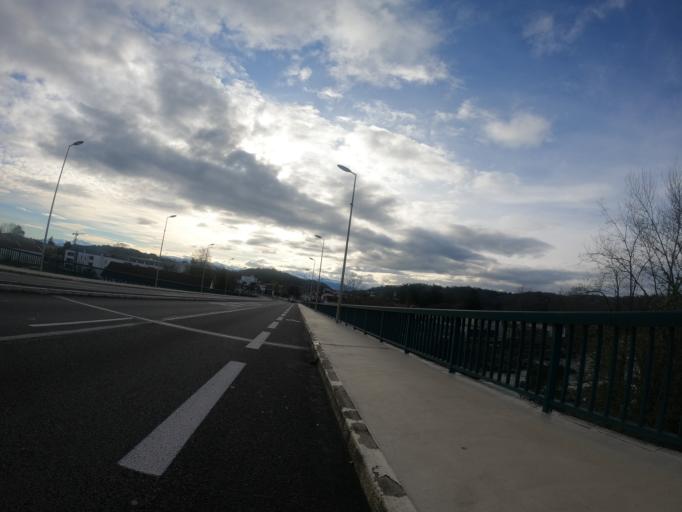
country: FR
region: Aquitaine
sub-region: Departement des Pyrenees-Atlantiques
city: Jurancon
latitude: 43.2946
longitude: -0.3871
